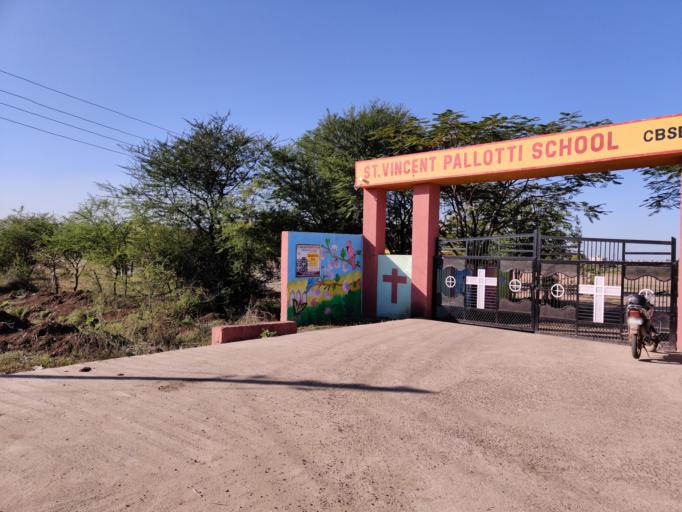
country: IN
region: Maharashtra
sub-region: Nagpur Division
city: Kamthi
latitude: 21.1992
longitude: 79.1676
